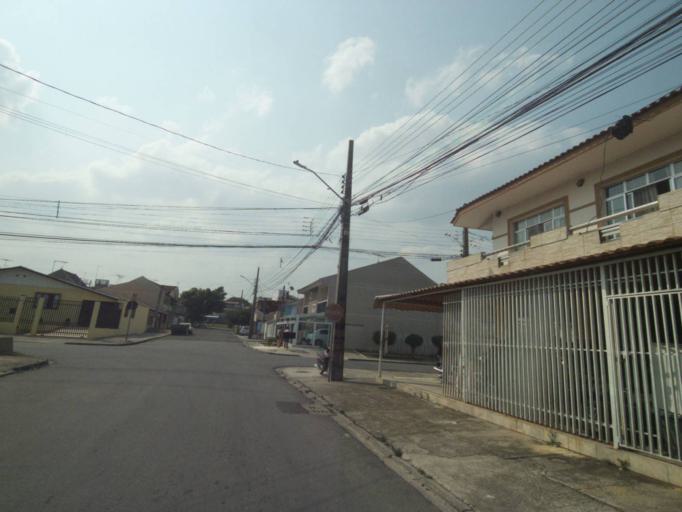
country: BR
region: Parana
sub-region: Sao Jose Dos Pinhais
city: Sao Jose dos Pinhais
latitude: -25.5277
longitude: -49.2355
